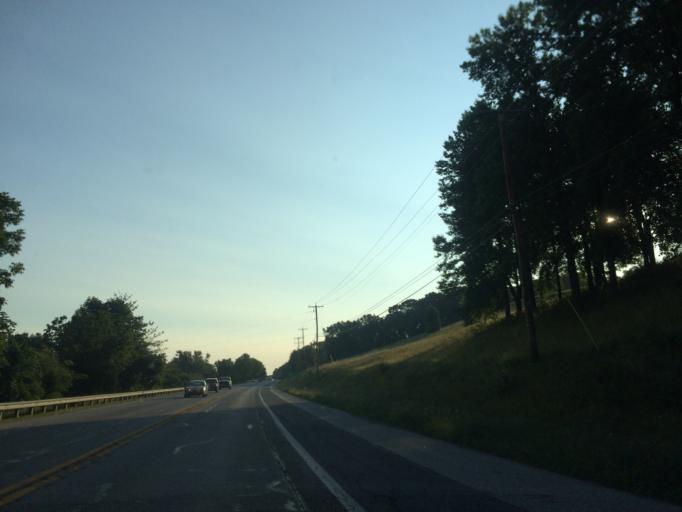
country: US
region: Maryland
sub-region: Carroll County
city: Manchester
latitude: 39.6395
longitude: -76.9223
